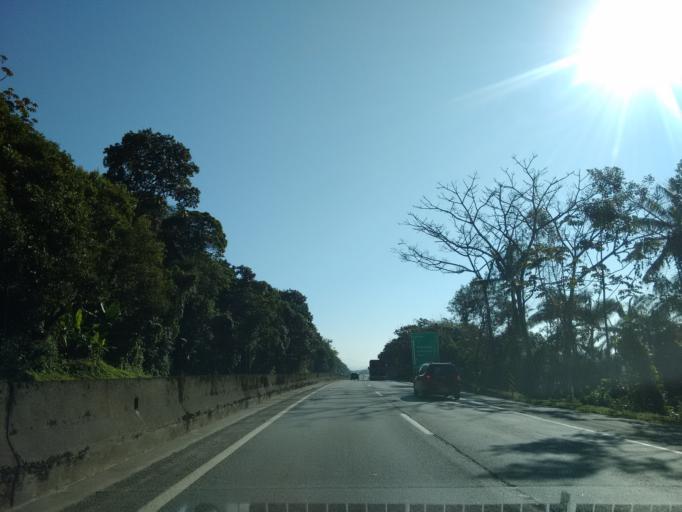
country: BR
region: Santa Catarina
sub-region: Joinville
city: Joinville
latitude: -26.2104
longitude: -48.9157
